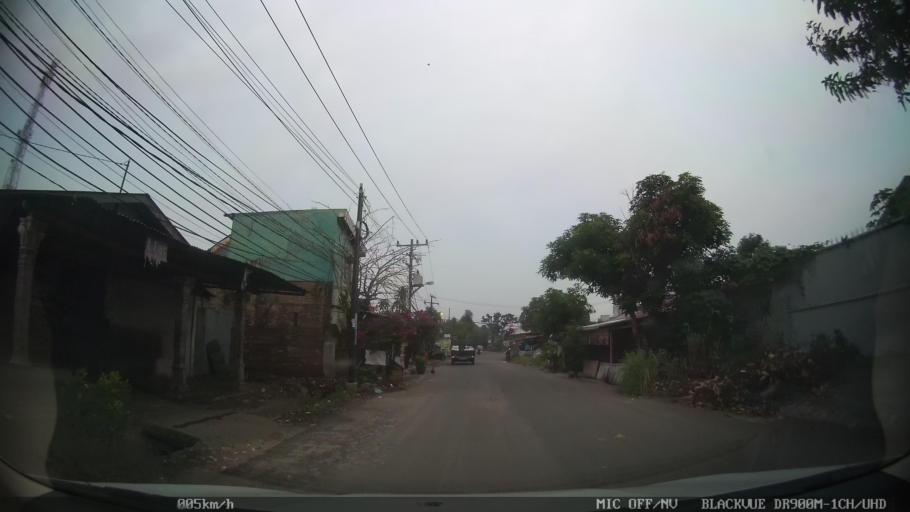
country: ID
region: North Sumatra
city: Deli Tua
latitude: 3.5371
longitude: 98.7316
